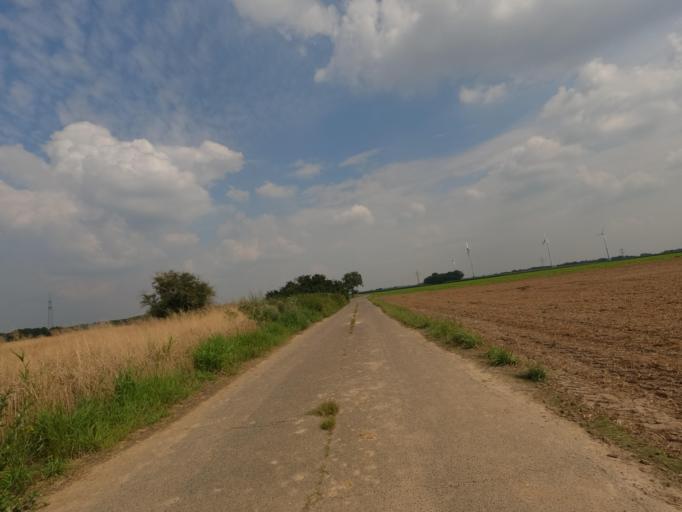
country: DE
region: North Rhine-Westphalia
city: Huckelhoven
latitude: 51.0109
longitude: 6.2076
